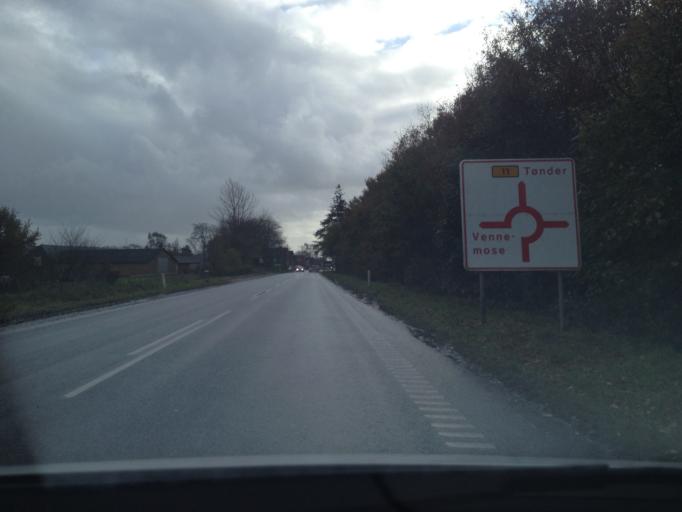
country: DK
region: South Denmark
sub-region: Tonder Kommune
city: Tonder
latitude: 54.9819
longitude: 8.8626
